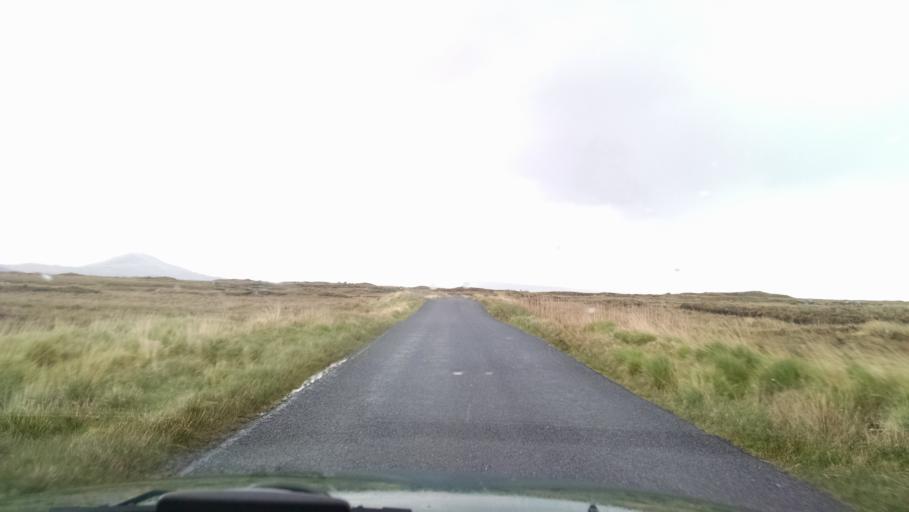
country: IE
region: Connaught
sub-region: County Galway
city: Clifden
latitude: 53.4382
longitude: -9.9173
